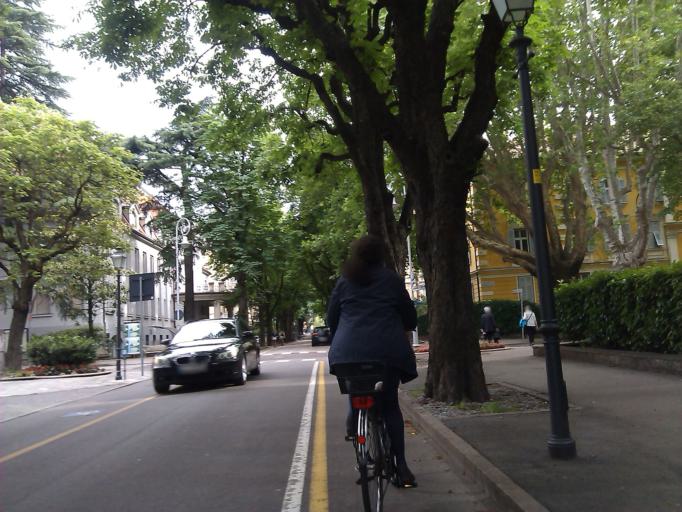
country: IT
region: Trentino-Alto Adige
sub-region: Bolzano
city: Merano
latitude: 46.6714
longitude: 11.1563
